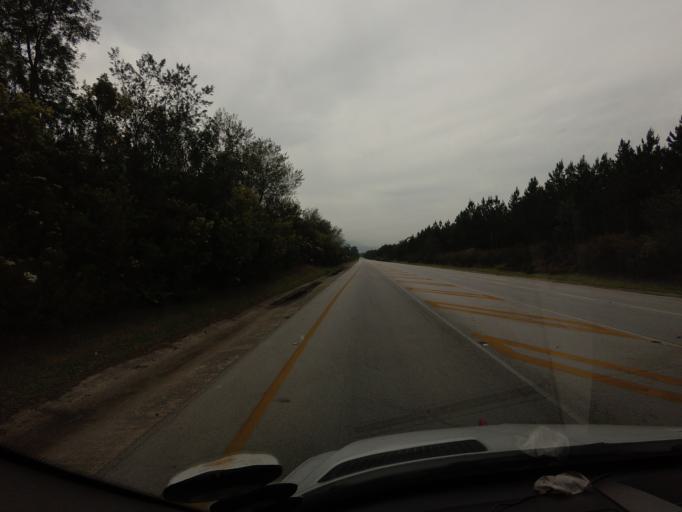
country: ZA
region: Eastern Cape
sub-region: Cacadu District Municipality
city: Kareedouw
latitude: -33.9710
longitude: 23.8402
